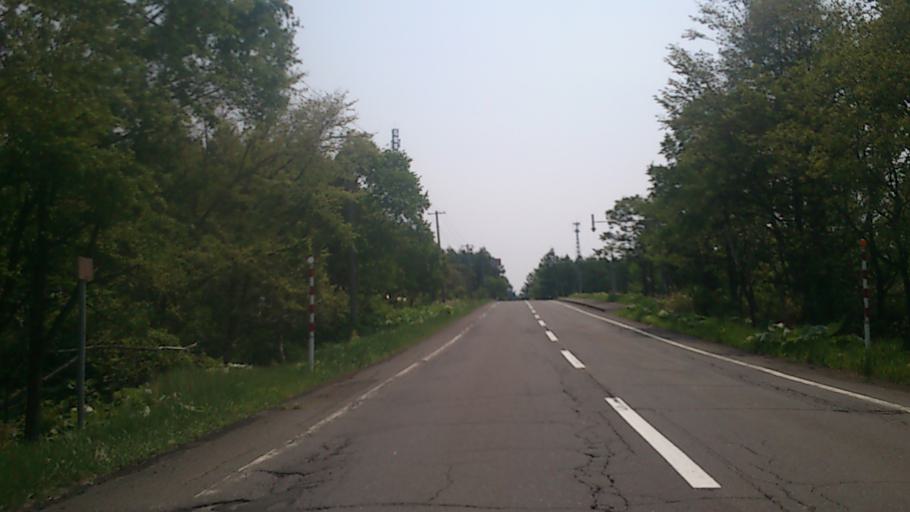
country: JP
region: Hokkaido
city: Shibetsu
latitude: 43.3659
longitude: 144.9791
